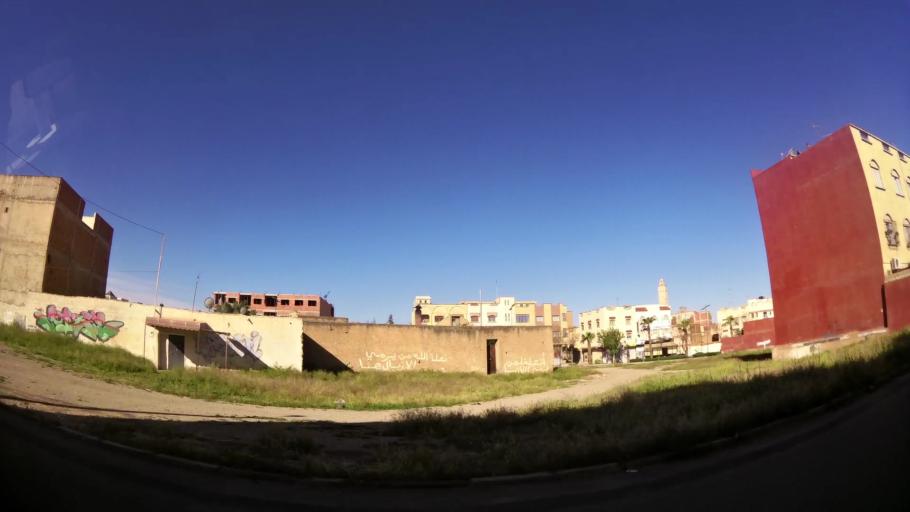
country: MA
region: Oriental
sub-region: Oujda-Angad
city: Oujda
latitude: 34.6601
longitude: -1.9028
